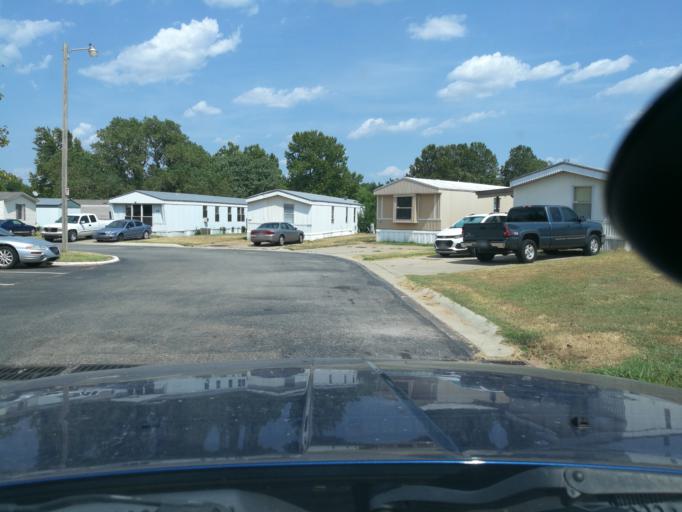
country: US
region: Oklahoma
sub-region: Oklahoma County
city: Del City
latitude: 35.4166
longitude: -97.4719
